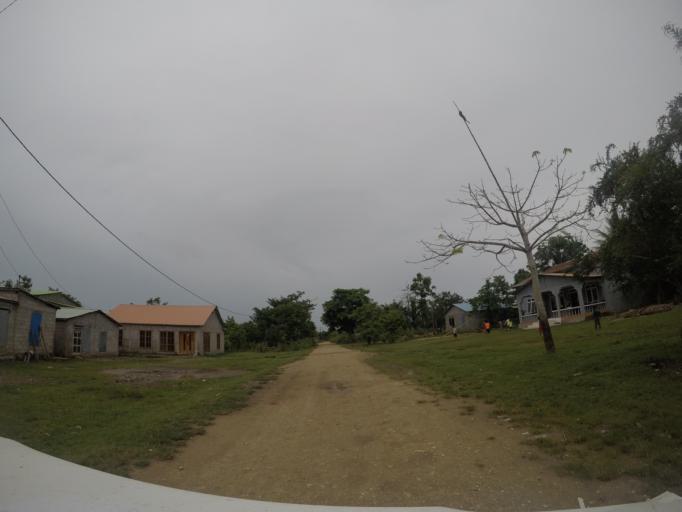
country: TL
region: Lautem
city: Lospalos
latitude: -8.5264
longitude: 127.0084
